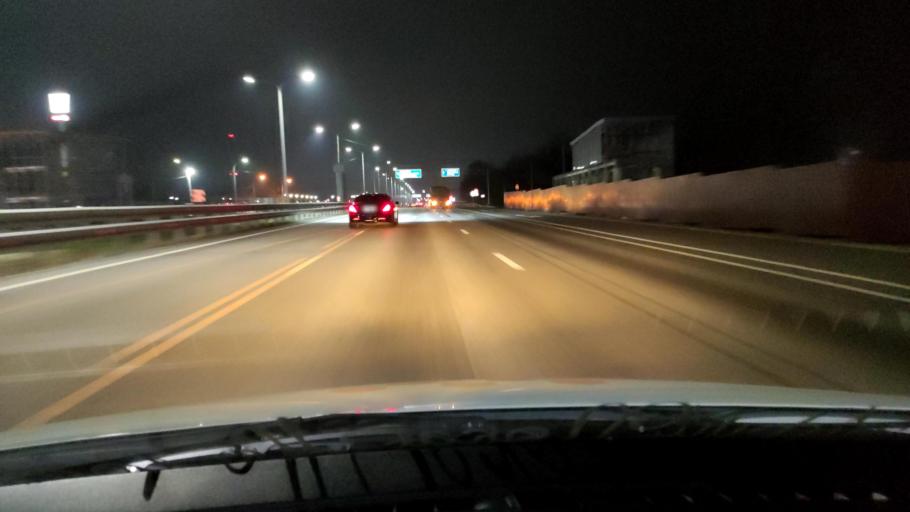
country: RU
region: Voronezj
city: Podgornoye
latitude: 51.8490
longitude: 39.2147
